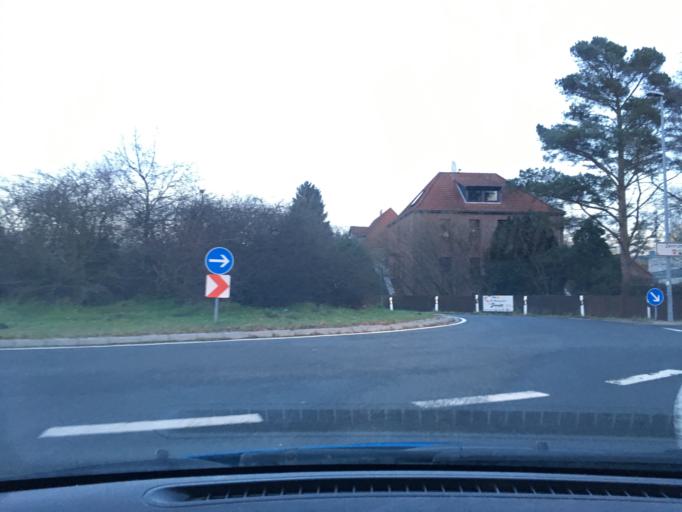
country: DE
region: Lower Saxony
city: Isernhagen Farster Bauerschaft
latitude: 52.5062
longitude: 9.8559
